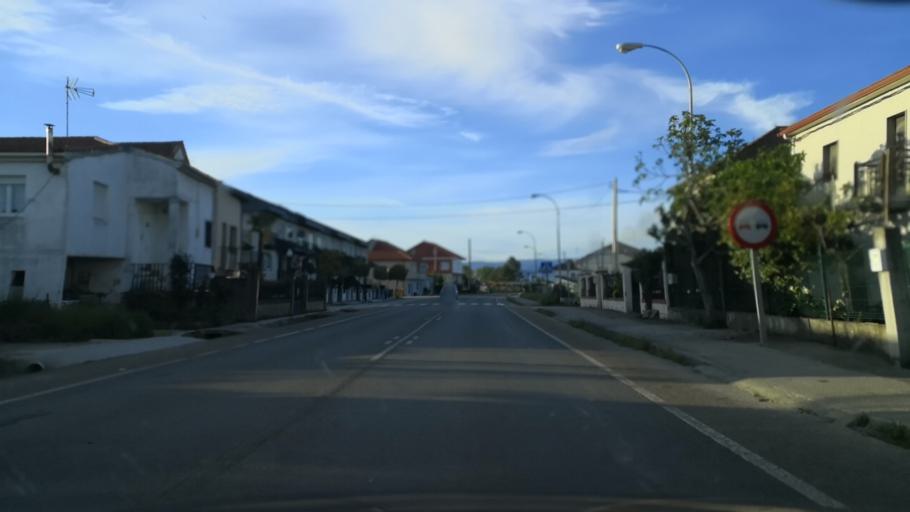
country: ES
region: Galicia
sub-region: Provincia de Ourense
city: Verin
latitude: 41.9206
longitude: -7.4437
